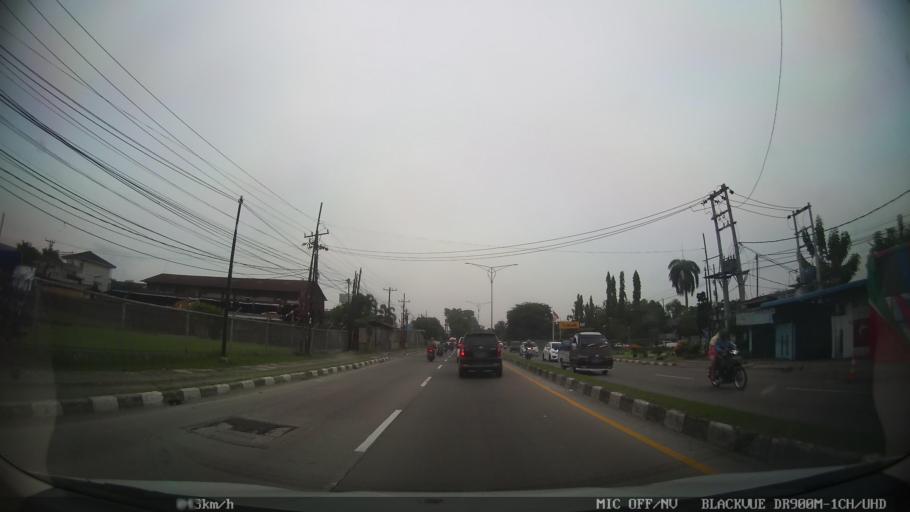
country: ID
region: North Sumatra
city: Deli Tua
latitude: 3.5326
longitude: 98.7276
